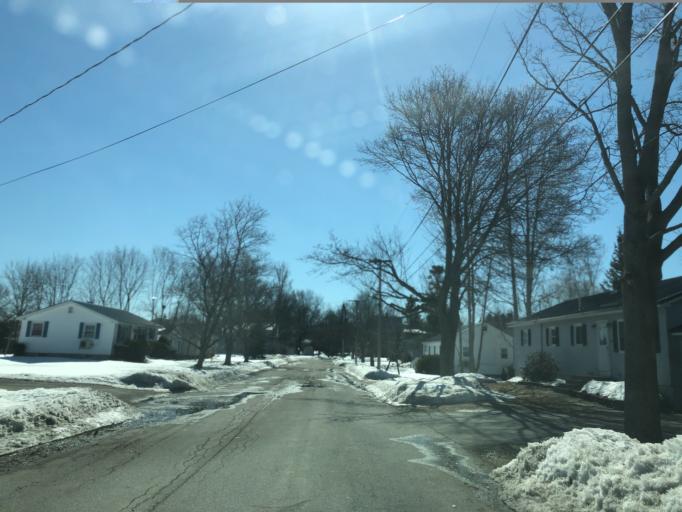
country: US
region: Maine
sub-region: Penobscot County
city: Brewer
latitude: 44.8200
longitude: -68.7555
